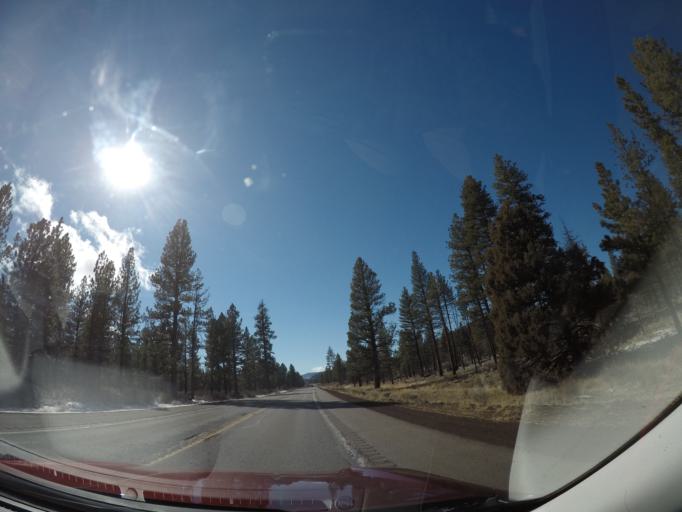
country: US
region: California
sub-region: Siskiyou County
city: Weed
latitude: 41.6727
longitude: -122.0775
